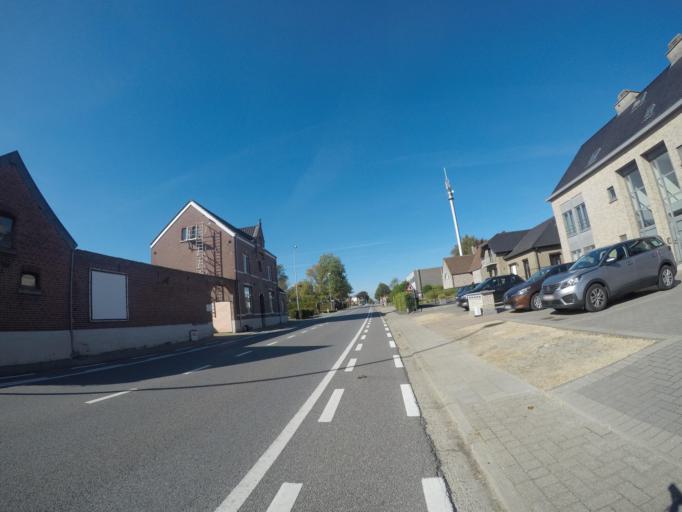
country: BE
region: Flanders
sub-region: Provincie Limburg
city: Alken
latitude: 50.8879
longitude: 5.2918
